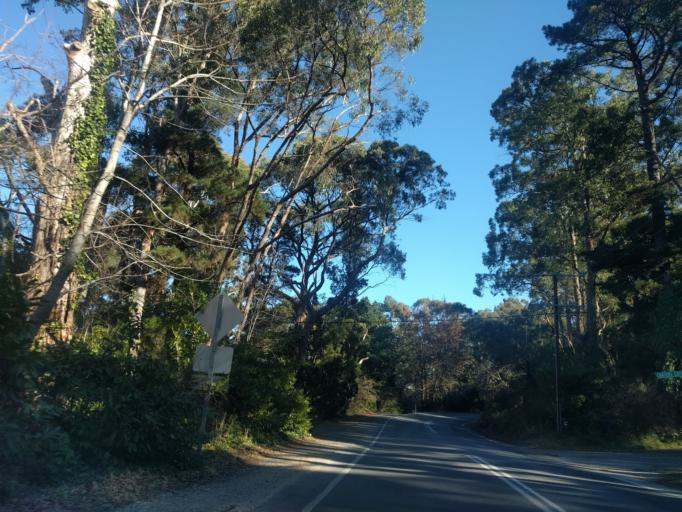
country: AU
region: South Australia
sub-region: Adelaide Hills
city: Crafers
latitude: -34.9941
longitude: 138.7122
